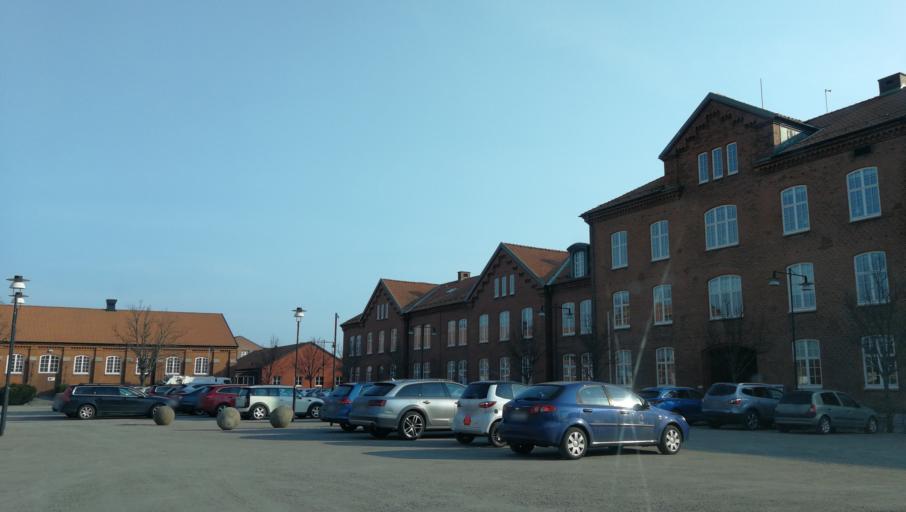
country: SE
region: Skane
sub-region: Ystads Kommun
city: Ystad
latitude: 55.4319
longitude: 13.8409
